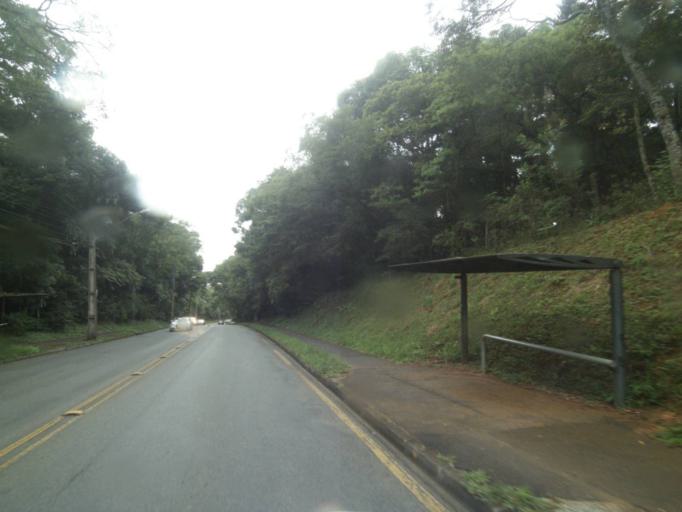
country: BR
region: Parana
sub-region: Curitiba
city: Curitiba
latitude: -25.4227
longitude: -49.3114
